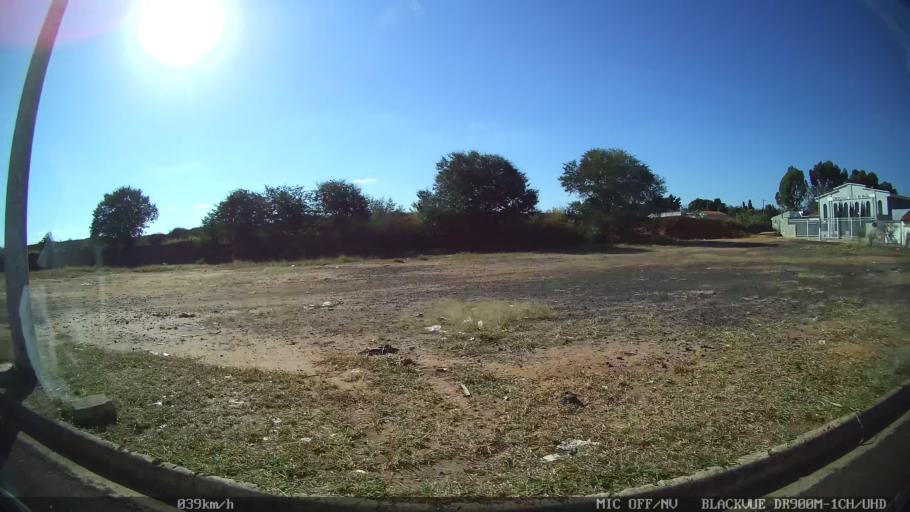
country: BR
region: Sao Paulo
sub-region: Franca
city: Franca
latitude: -20.4780
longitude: -47.4169
